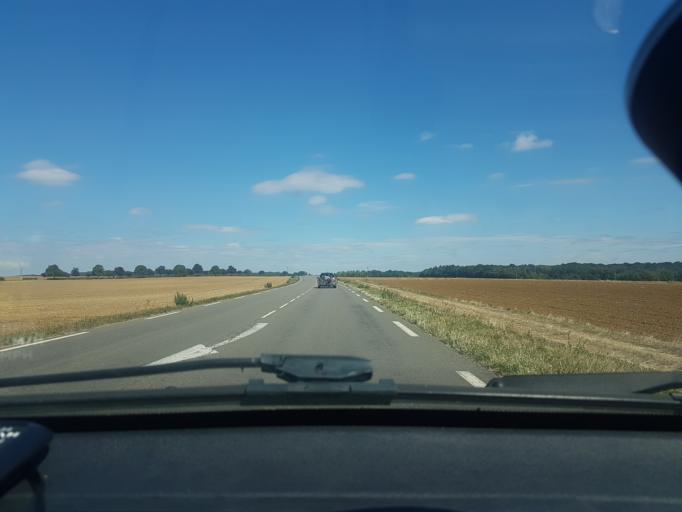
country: FR
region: Bourgogne
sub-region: Departement de la Cote-d'Or
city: Arc-sur-Tille
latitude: 47.3542
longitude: 5.2076
